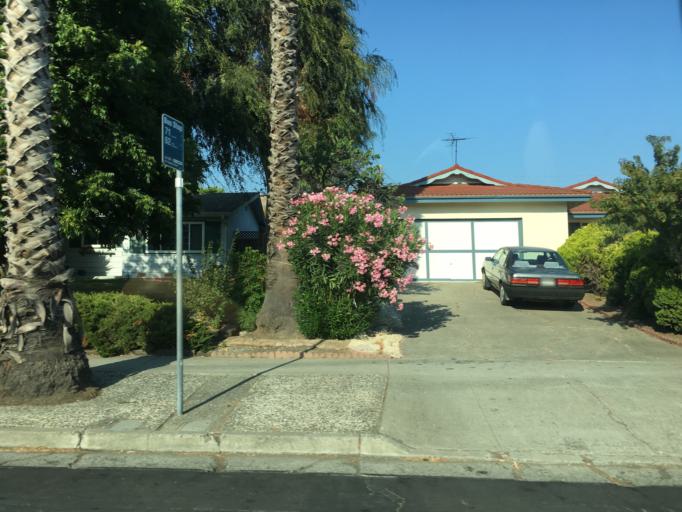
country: US
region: California
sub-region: Santa Clara County
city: East Foothills
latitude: 37.3968
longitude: -121.8455
